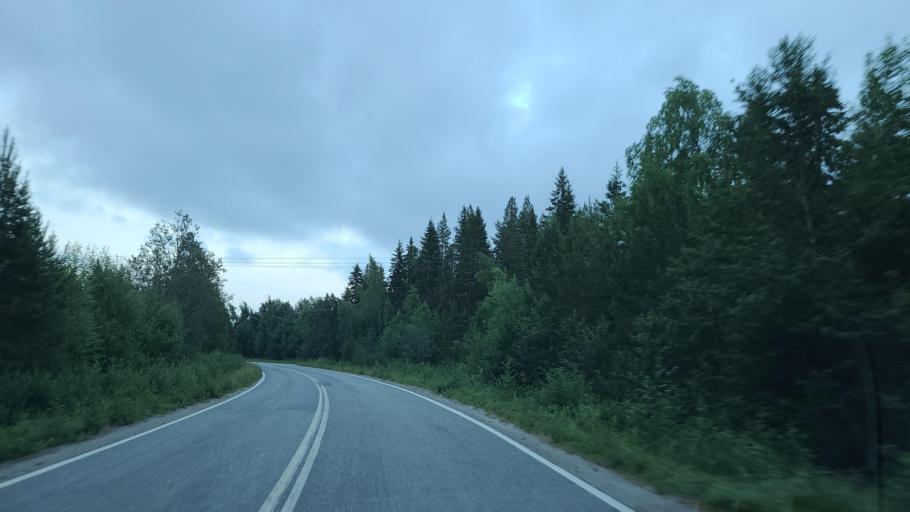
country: FI
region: Ostrobothnia
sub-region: Vaasa
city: Replot
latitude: 63.2747
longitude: 21.1389
